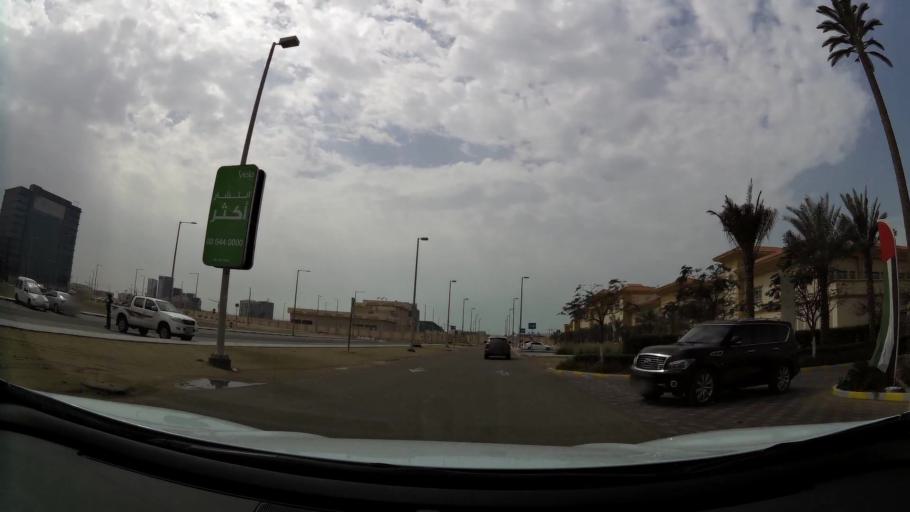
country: AE
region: Abu Dhabi
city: Abu Dhabi
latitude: 24.4311
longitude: 54.4628
